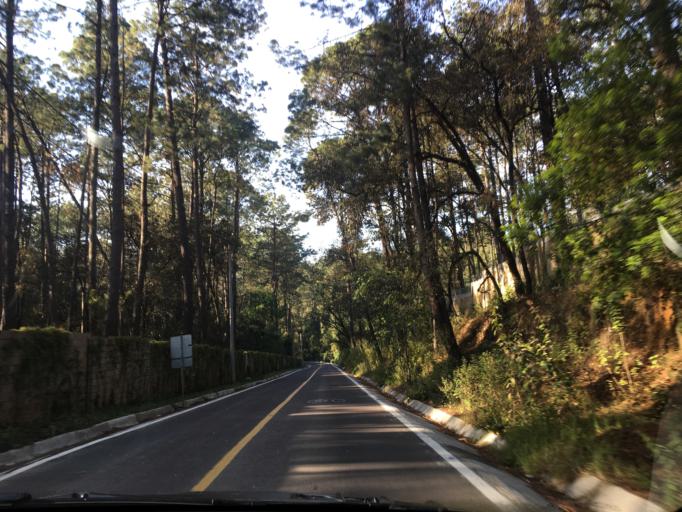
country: MX
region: Mexico
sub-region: Valle de Bravo
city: Casas Viejas
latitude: 19.1492
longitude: -100.1261
